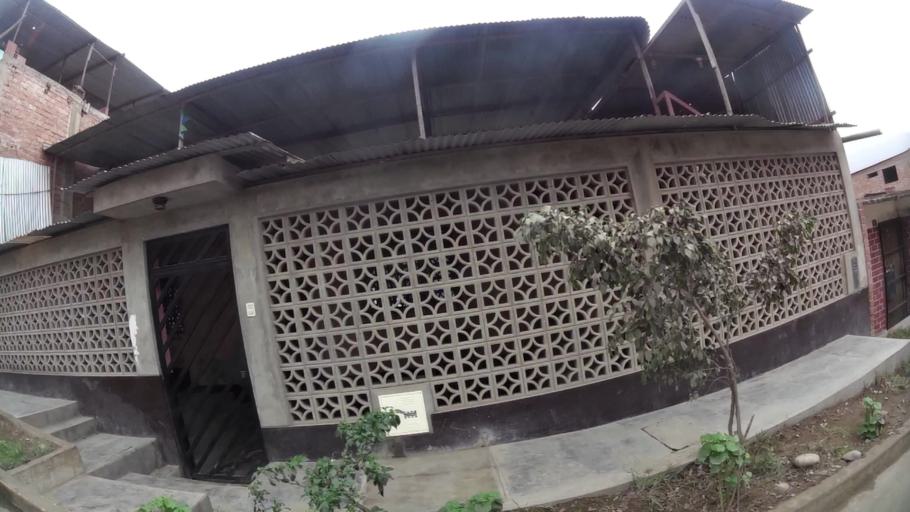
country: PE
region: Lima
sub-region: Lima
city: Surco
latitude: -12.2103
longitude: -76.9138
